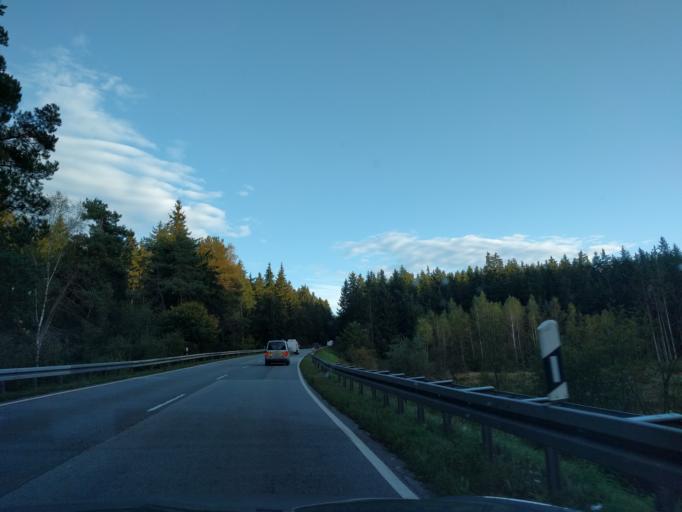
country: DE
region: Bavaria
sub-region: Lower Bavaria
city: Viechtach
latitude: 49.0519
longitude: 12.9239
